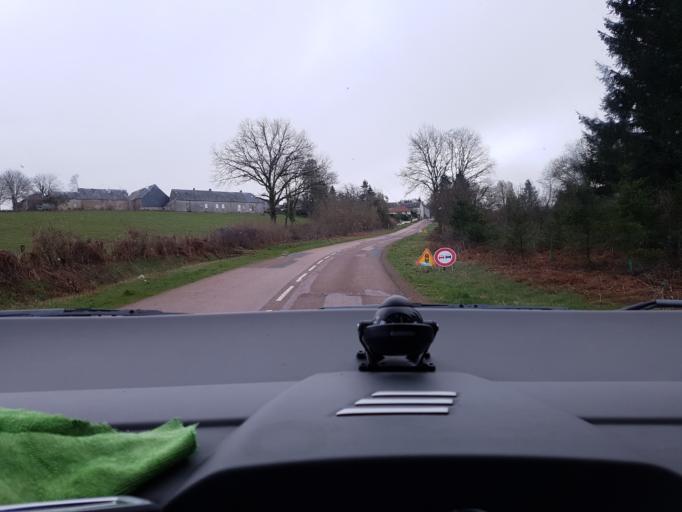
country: FR
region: Bourgogne
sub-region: Departement de la Cote-d'Or
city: Saulieu
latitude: 47.2730
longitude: 4.0287
